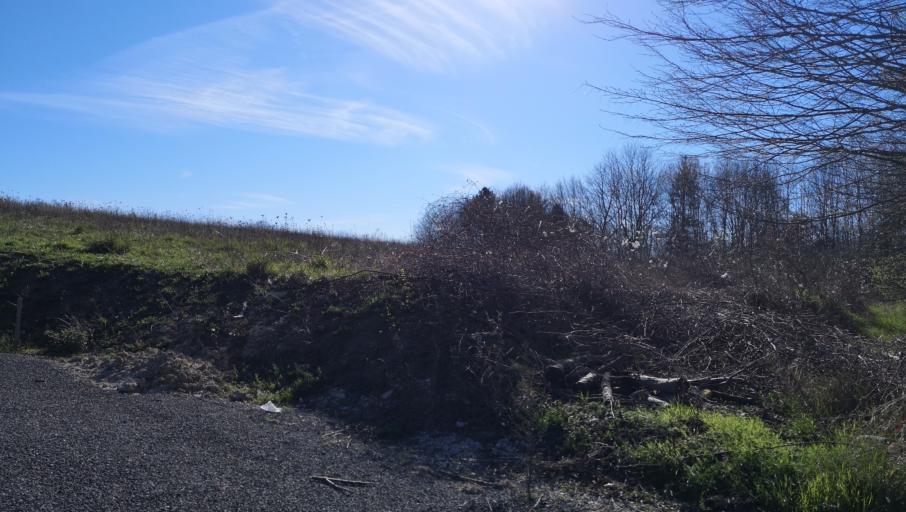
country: FR
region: Centre
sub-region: Departement du Loiret
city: Saint-Jean-de-Braye
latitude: 47.9027
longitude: 1.9862
